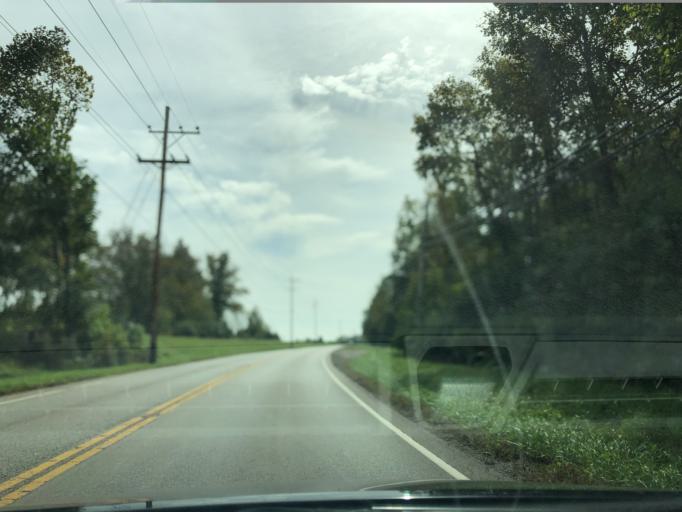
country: US
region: Ohio
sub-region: Clermont County
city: Milford
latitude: 39.2080
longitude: -84.2908
